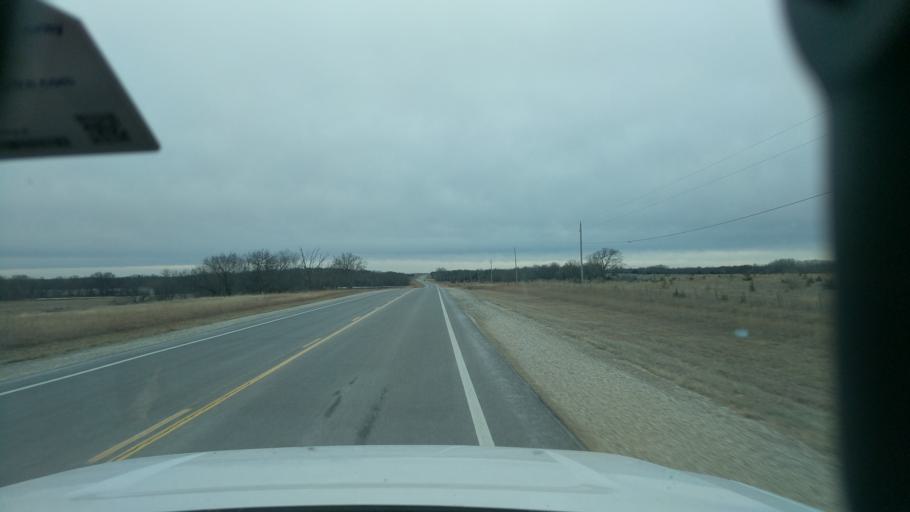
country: US
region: Kansas
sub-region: Marion County
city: Marion
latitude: 38.4787
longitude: -96.9578
